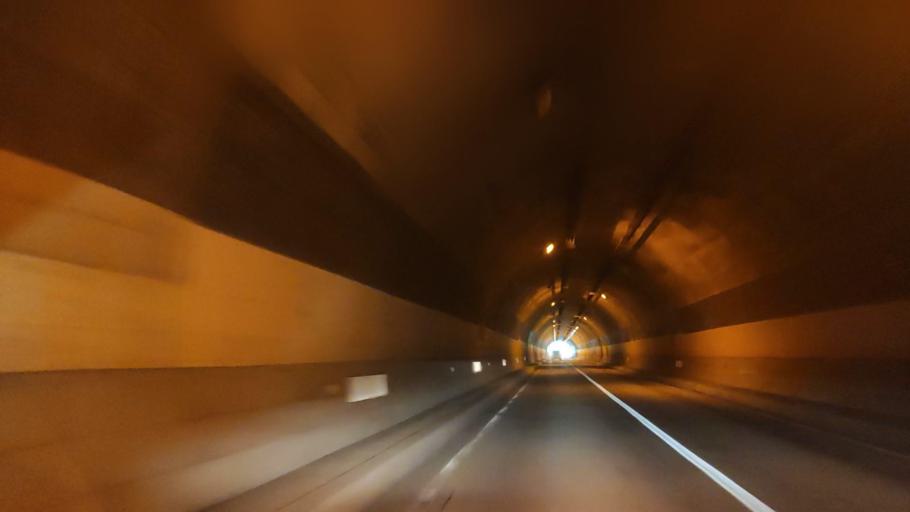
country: JP
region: Hokkaido
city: Bibai
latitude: 43.1649
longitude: 142.0815
